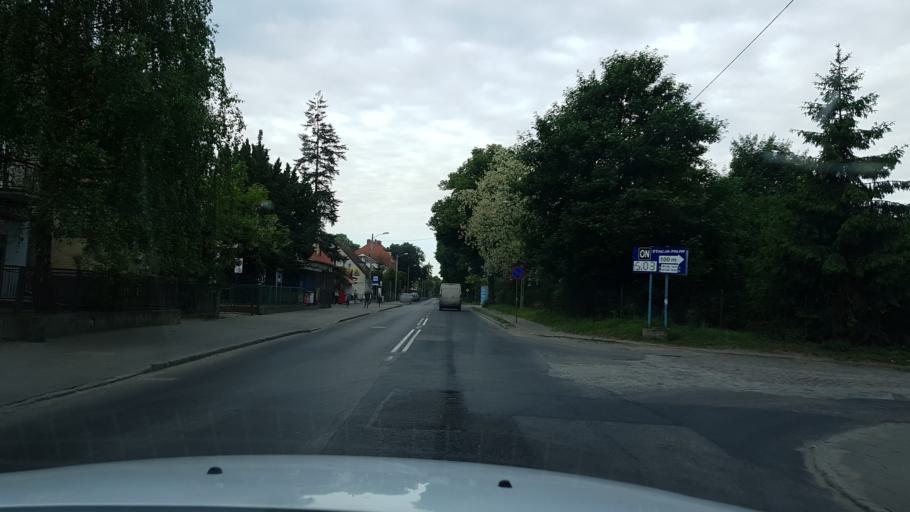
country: PL
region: West Pomeranian Voivodeship
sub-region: Szczecin
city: Szczecin
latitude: 53.3649
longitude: 14.5927
